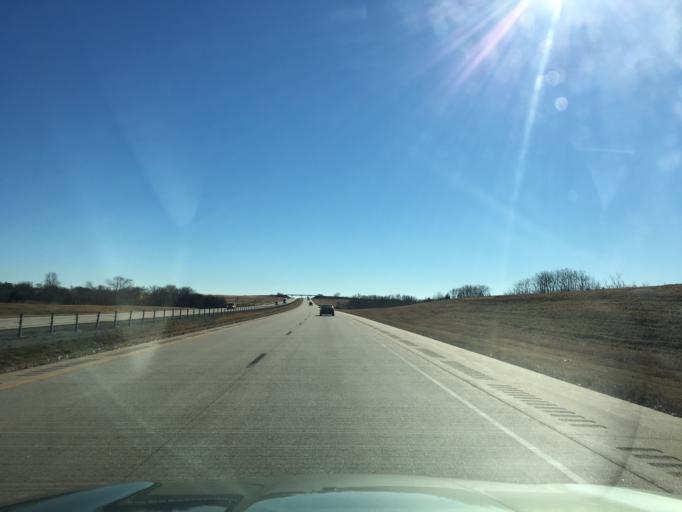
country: US
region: Oklahoma
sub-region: Kay County
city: Tonkawa
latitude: 36.5015
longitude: -97.3349
